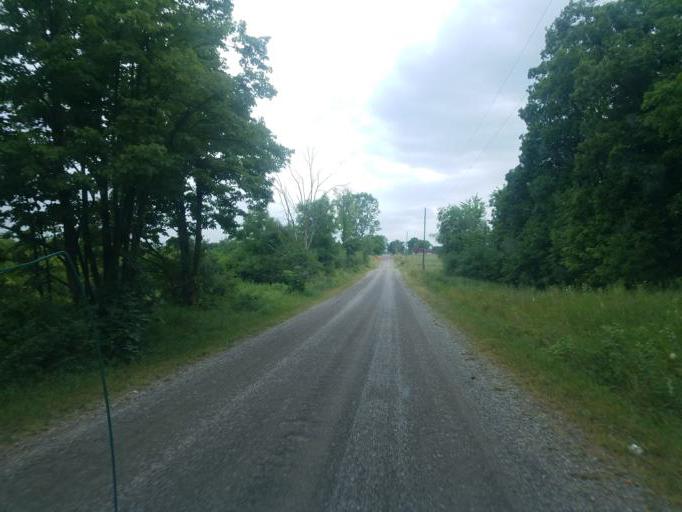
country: US
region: Ohio
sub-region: Defiance County
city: Hicksville
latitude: 41.3117
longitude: -84.8039
